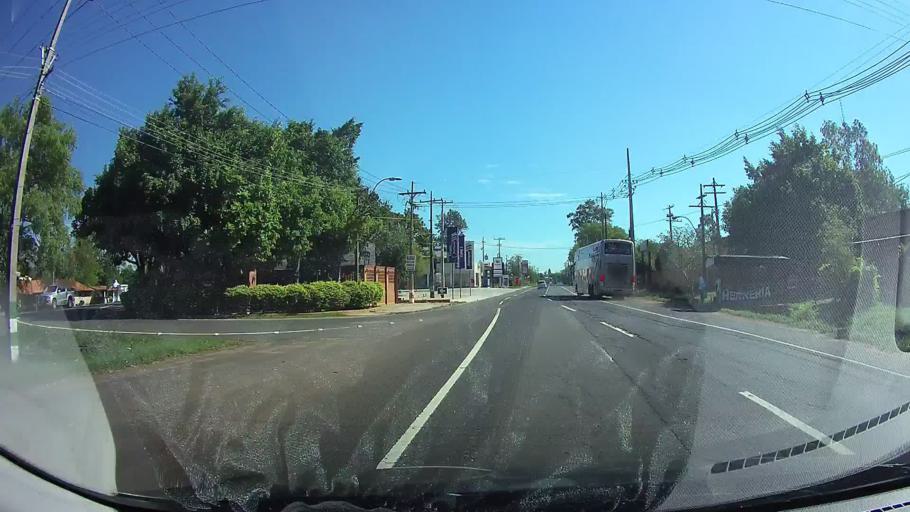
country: PY
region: Central
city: Ypacarai
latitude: -25.3934
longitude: -57.2777
